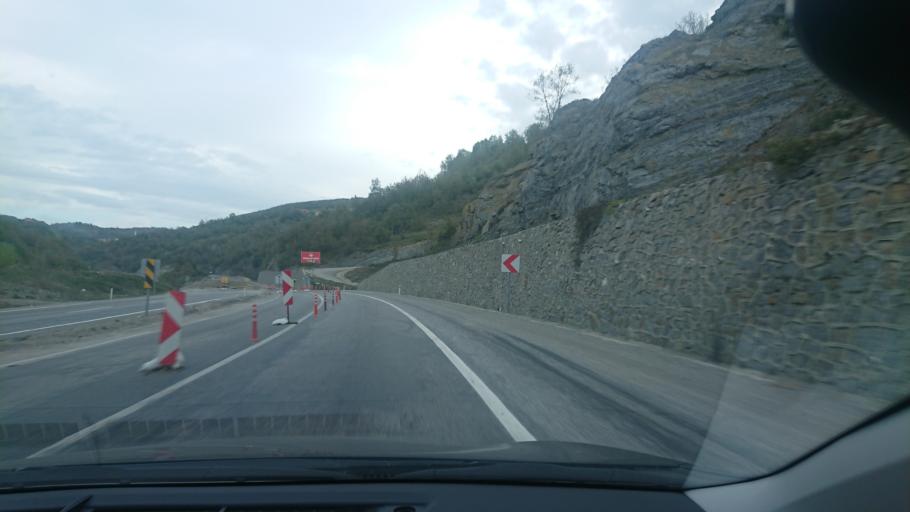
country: TR
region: Zonguldak
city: Beycuma
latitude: 41.4000
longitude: 31.9377
